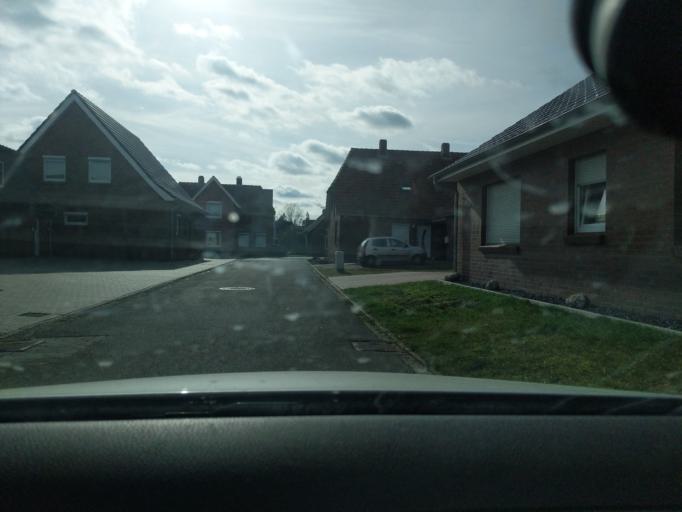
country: DE
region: Lower Saxony
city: Drochtersen
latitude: 53.7099
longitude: 9.3893
